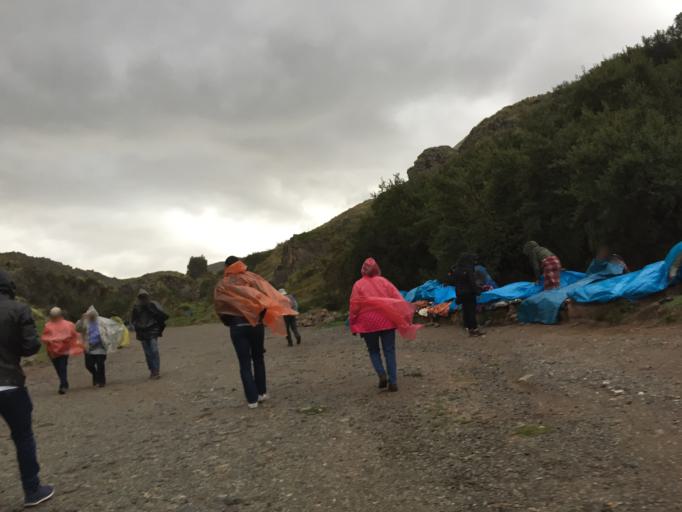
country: PE
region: Cusco
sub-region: Provincia de Cusco
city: Cusco
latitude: -13.4793
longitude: -71.9664
